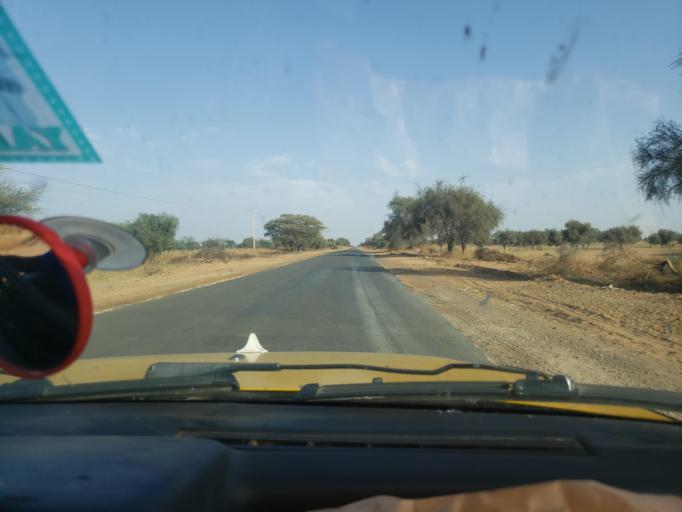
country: SN
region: Louga
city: Louga
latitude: 15.5045
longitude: -15.9550
